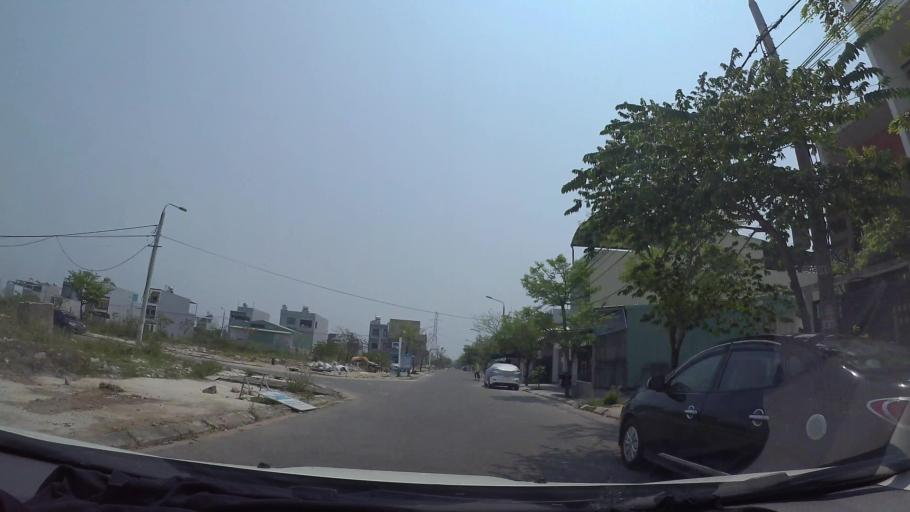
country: VN
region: Da Nang
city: Cam Le
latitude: 16.0126
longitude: 108.2200
